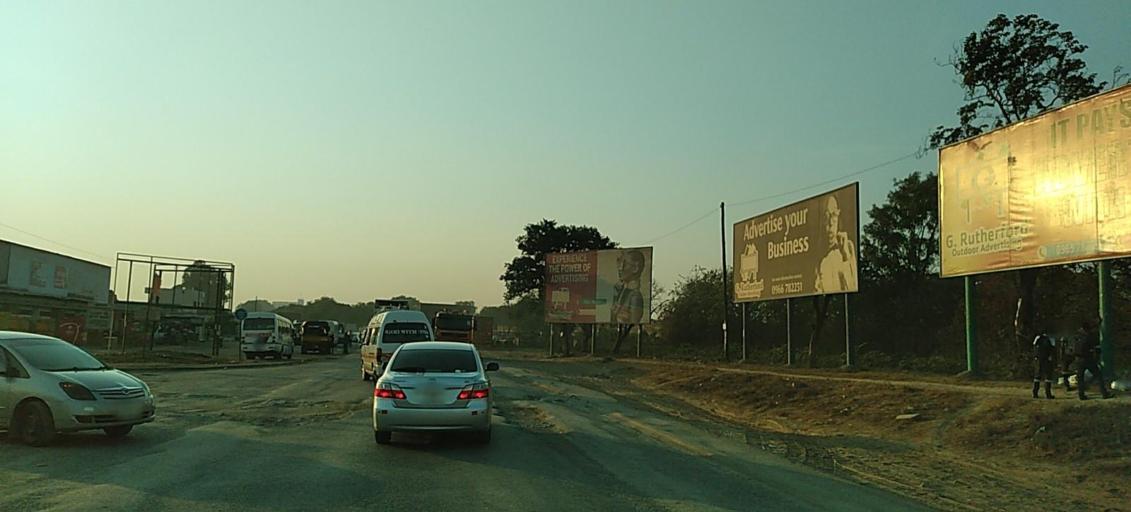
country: ZM
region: Copperbelt
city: Ndola
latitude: -13.0083
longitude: 28.6533
